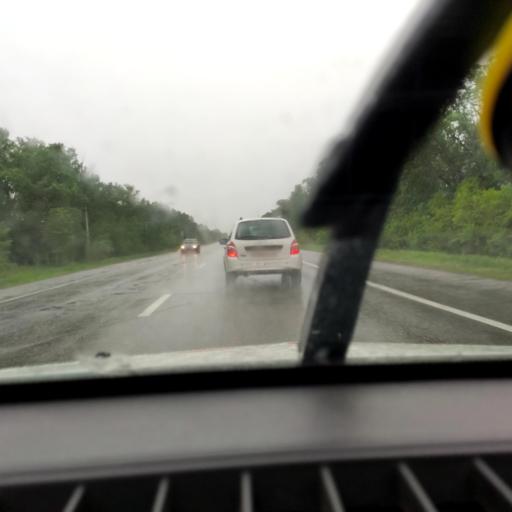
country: RU
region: Samara
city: Tol'yatti
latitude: 53.5941
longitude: 49.4072
